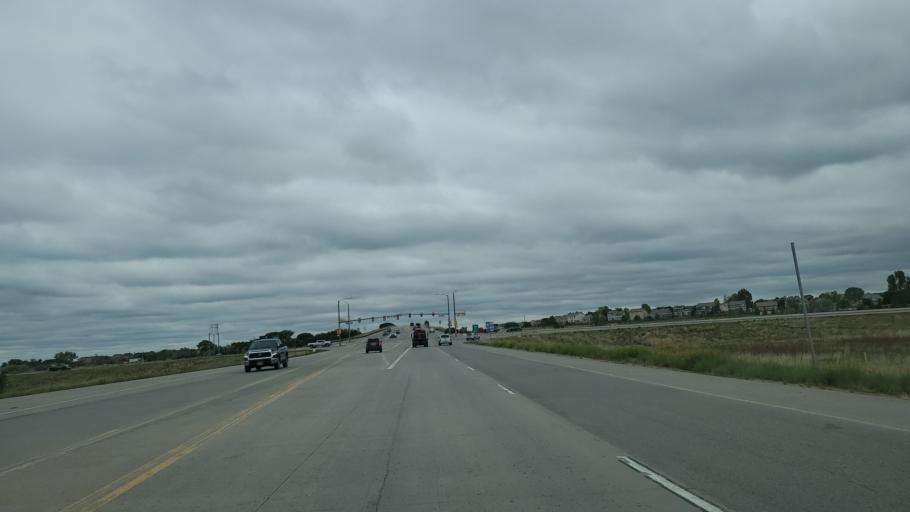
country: US
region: Colorado
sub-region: Adams County
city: Brighton
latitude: 39.9143
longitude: -104.8217
